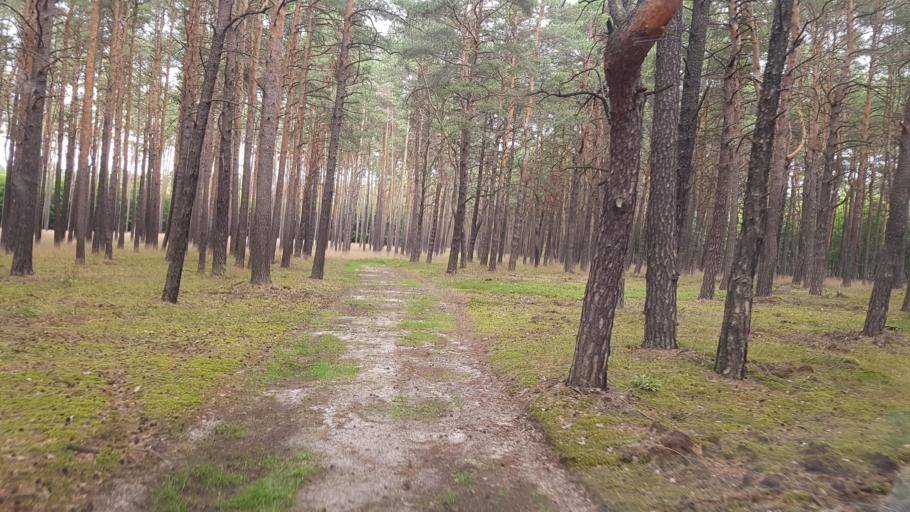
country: DE
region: Brandenburg
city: Crinitz
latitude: 51.7133
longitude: 13.7282
